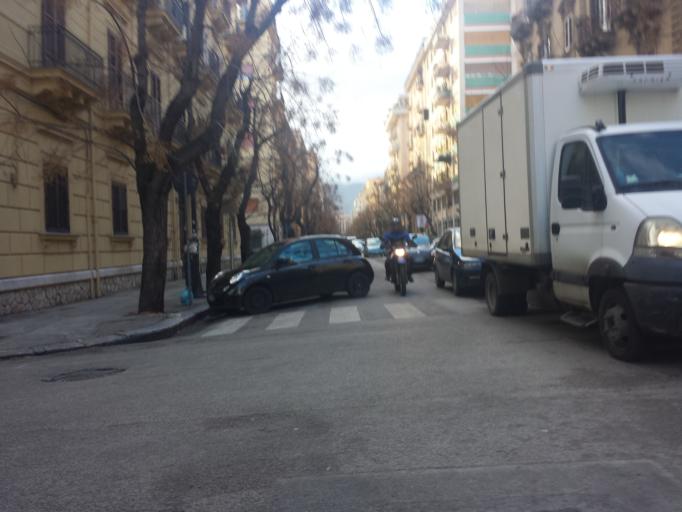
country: IT
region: Sicily
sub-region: Palermo
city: Palermo
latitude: 38.1291
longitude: 13.3510
